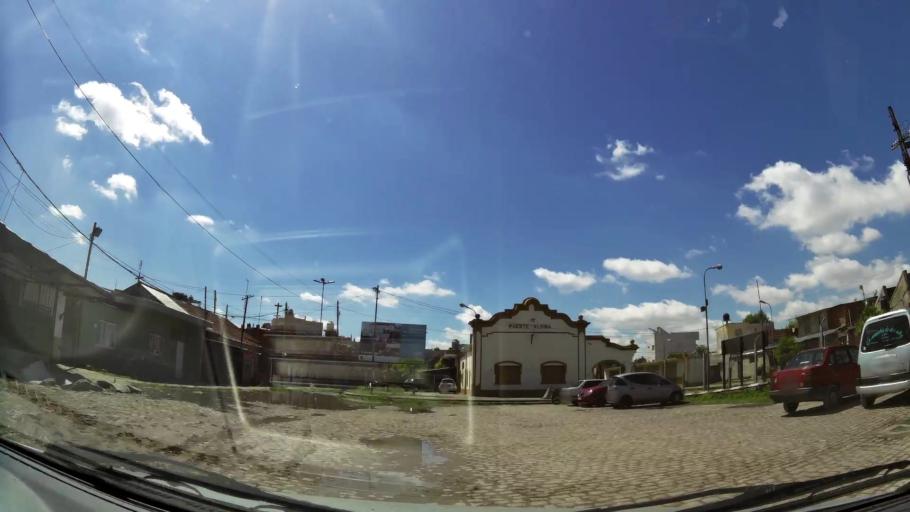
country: AR
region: Buenos Aires
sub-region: Partido de Lanus
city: Lanus
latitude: -34.6609
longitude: -58.4162
